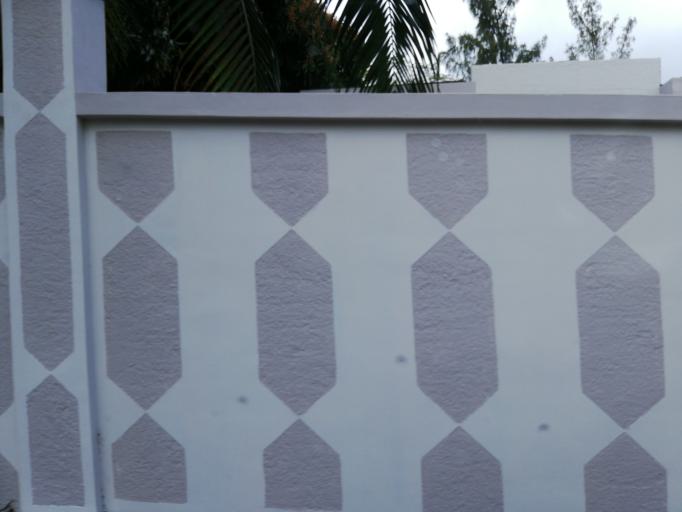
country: MU
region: Moka
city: Pailles
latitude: -20.2053
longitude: 57.4723
